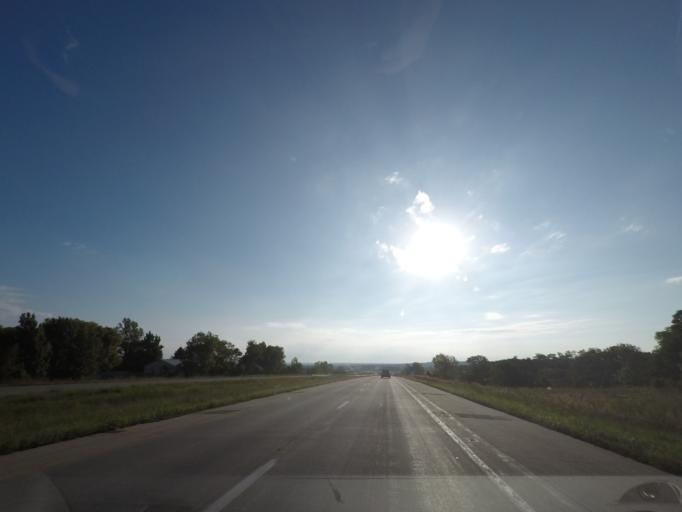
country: US
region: Iowa
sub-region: Warren County
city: Carlisle
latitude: 41.5116
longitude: -93.5416
